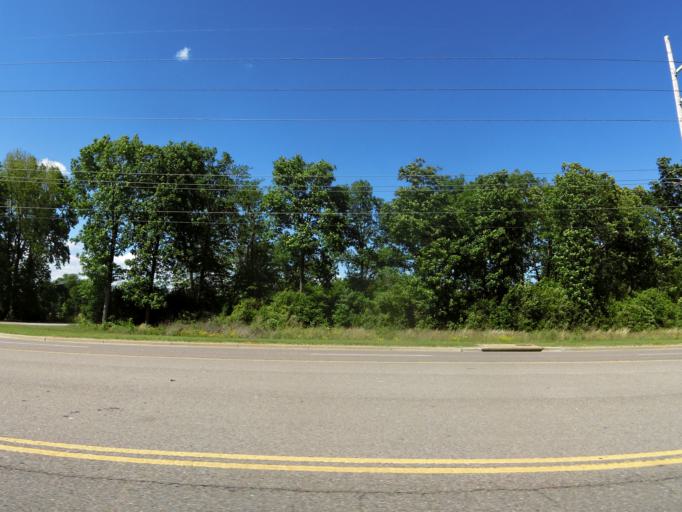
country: US
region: South Carolina
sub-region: Aiken County
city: Aiken
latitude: 33.5441
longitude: -81.6753
